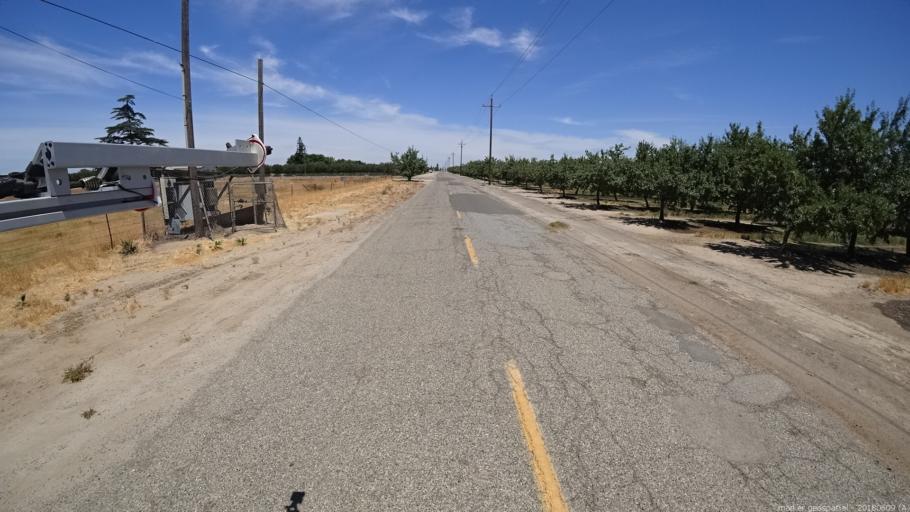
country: US
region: California
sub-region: Madera County
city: Parkwood
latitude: 36.9286
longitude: -120.0833
